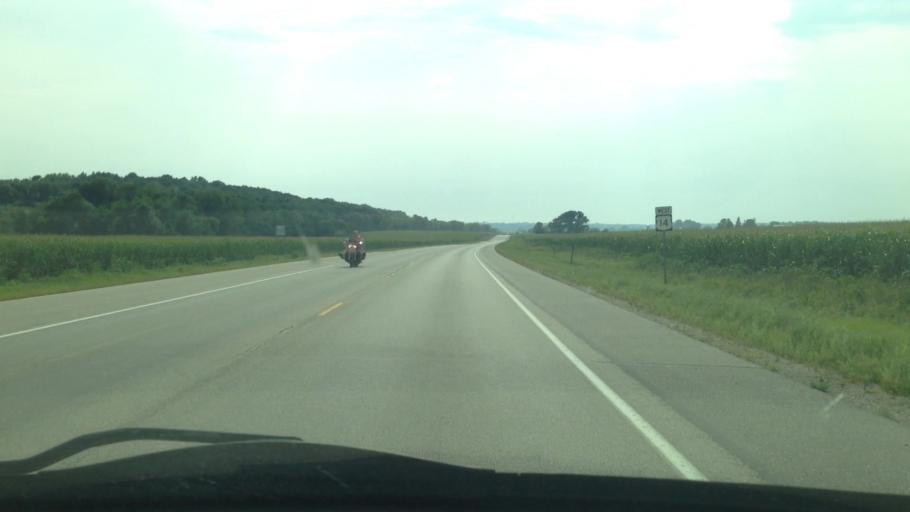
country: US
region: Minnesota
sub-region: Winona County
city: Lewiston
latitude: 43.9767
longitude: -91.9600
